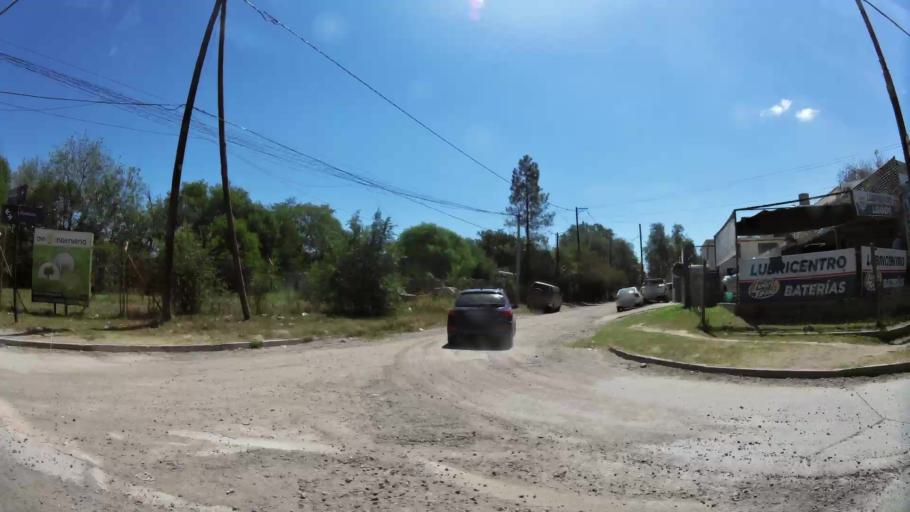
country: AR
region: Cordoba
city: Villa Allende
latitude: -31.3352
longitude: -64.2744
